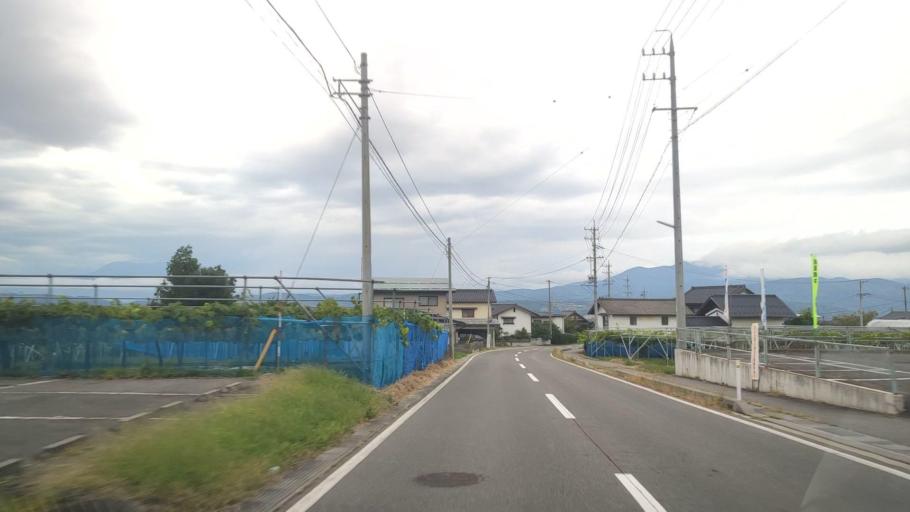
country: JP
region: Nagano
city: Nakano
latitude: 36.7635
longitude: 138.3837
